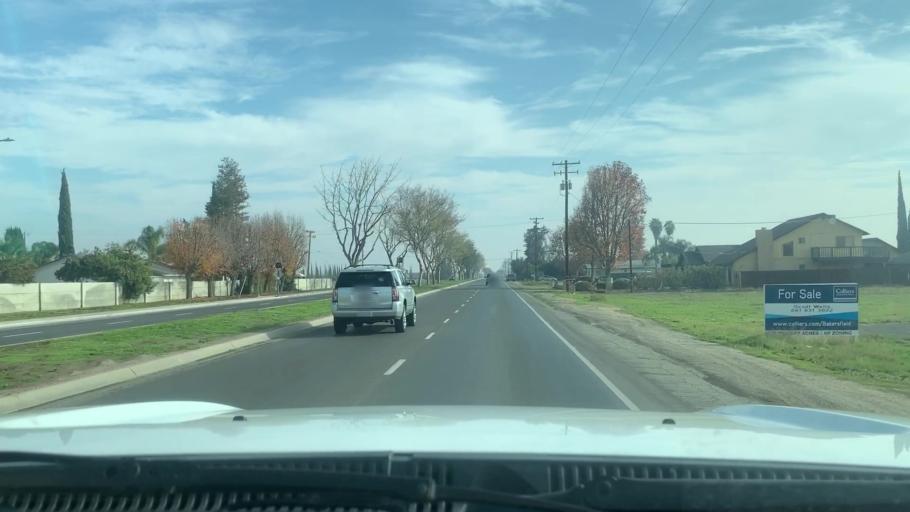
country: US
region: California
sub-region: Kern County
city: Shafter
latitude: 35.4998
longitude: -119.2585
